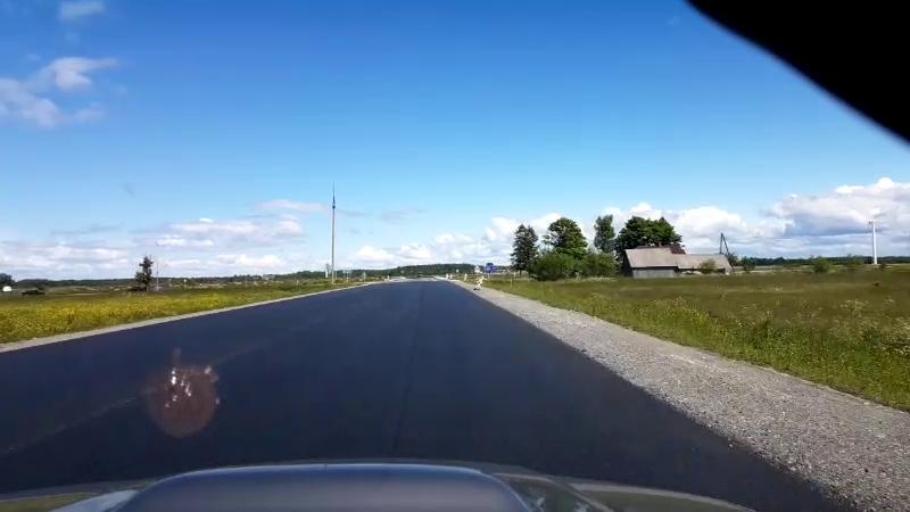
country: LV
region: Salacgrivas
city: Ainazi
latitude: 57.8628
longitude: 24.3698
